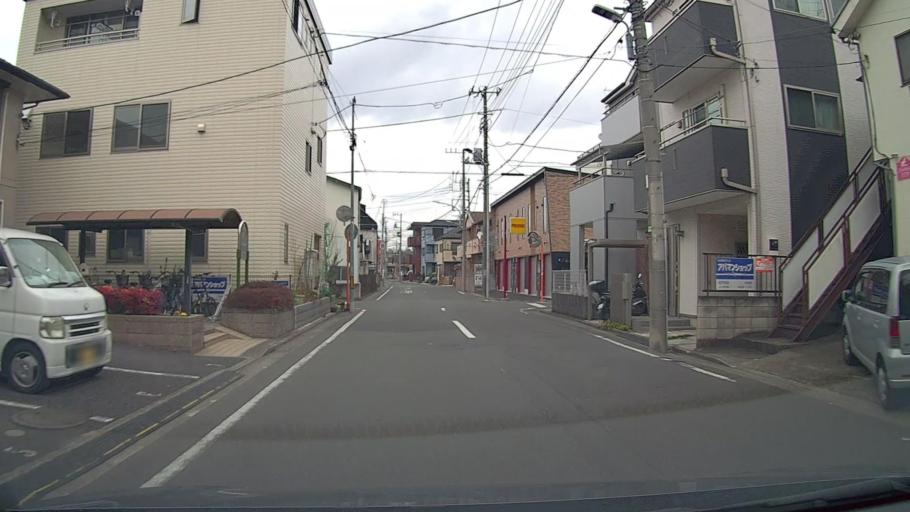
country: JP
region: Saitama
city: Shimotoda
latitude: 35.8153
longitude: 139.6545
